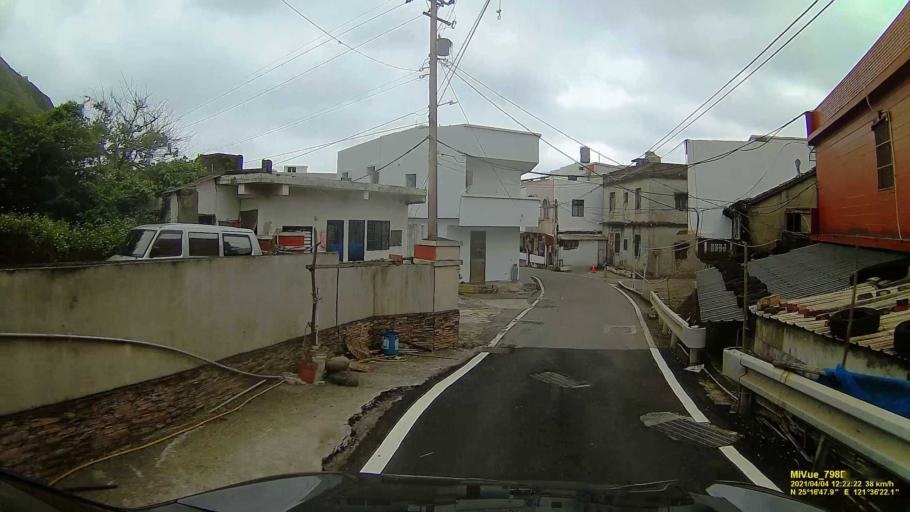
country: TW
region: Taiwan
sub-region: Keelung
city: Keelung
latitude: 25.2802
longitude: 121.6063
